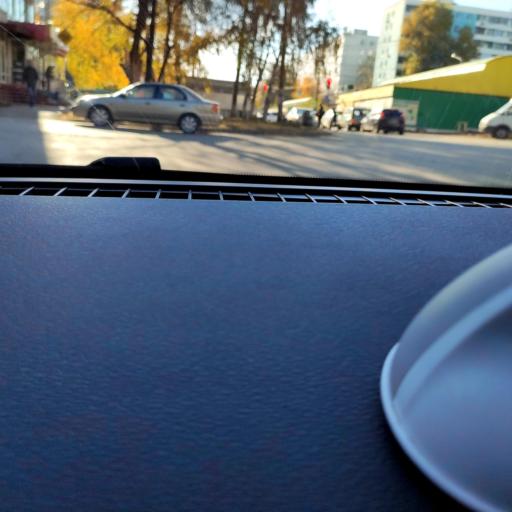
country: RU
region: Samara
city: Samara
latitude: 53.2386
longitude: 50.2174
